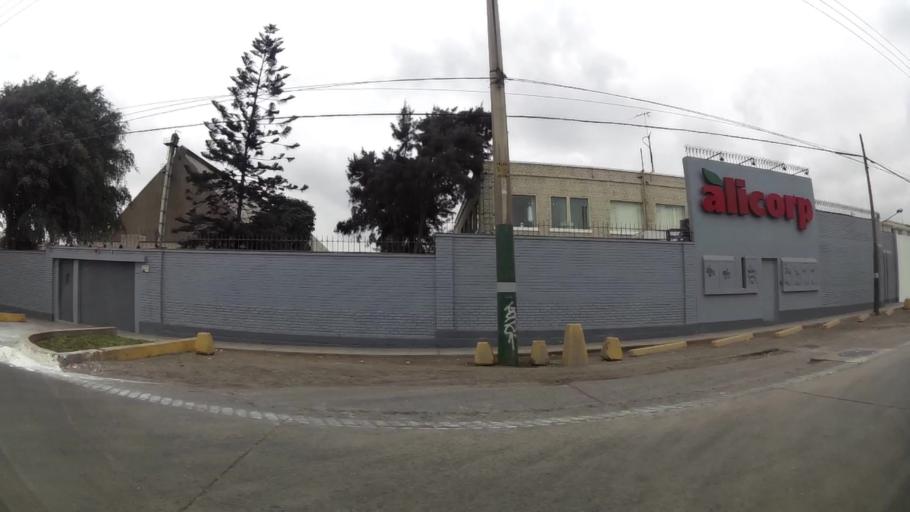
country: PE
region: Callao
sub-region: Callao
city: Callao
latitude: -12.0480
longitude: -77.0948
